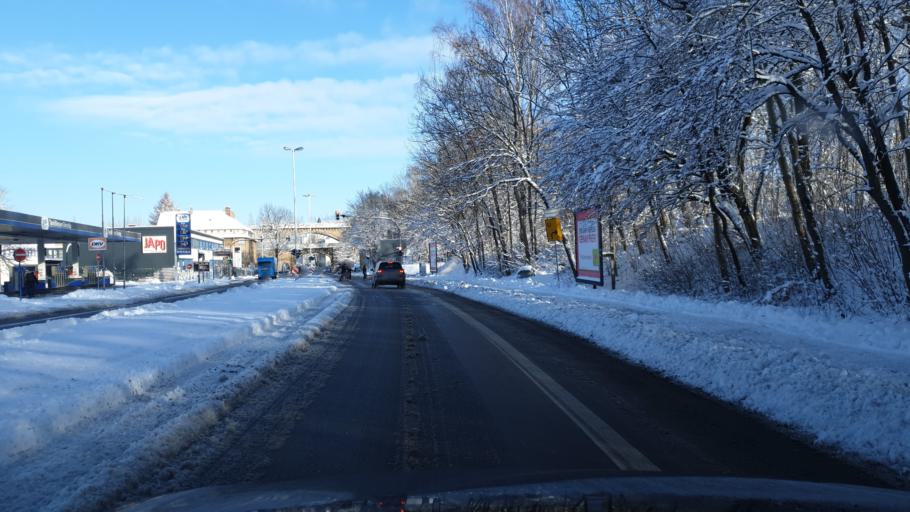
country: DE
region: Saxony
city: Chemnitz
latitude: 50.8518
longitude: 12.9293
